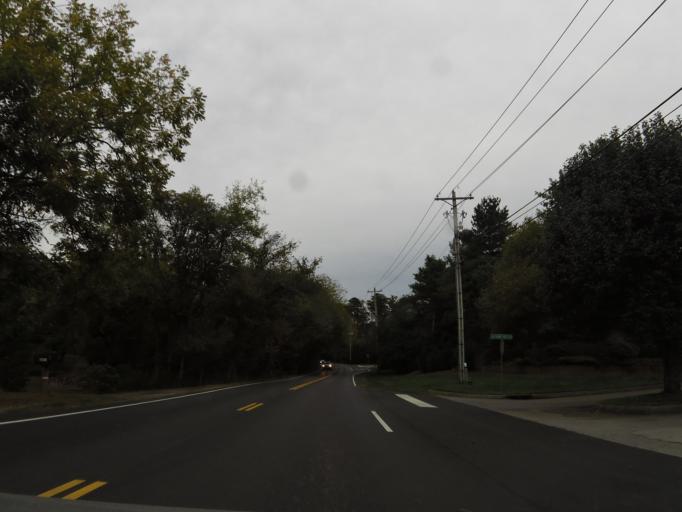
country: US
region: Tennessee
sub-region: Blount County
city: Louisville
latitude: 35.8754
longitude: -84.0447
